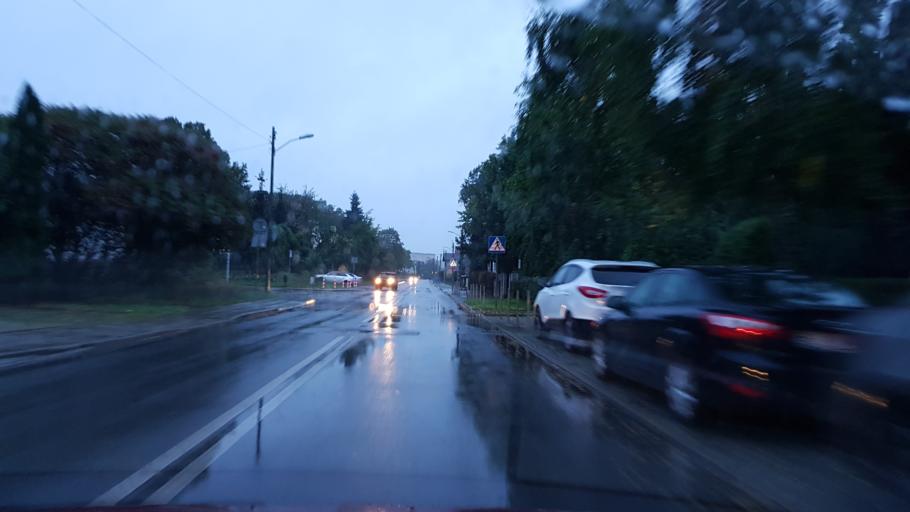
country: PL
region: West Pomeranian Voivodeship
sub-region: Powiat policki
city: Przeclaw
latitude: 53.4145
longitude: 14.4946
